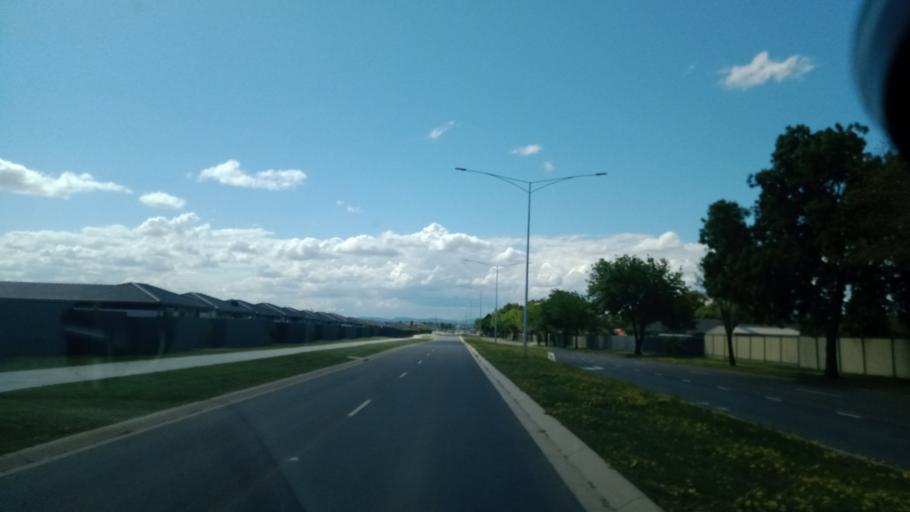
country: AU
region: Victoria
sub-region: Casey
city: Cranbourne West
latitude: -38.1068
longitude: 145.2527
